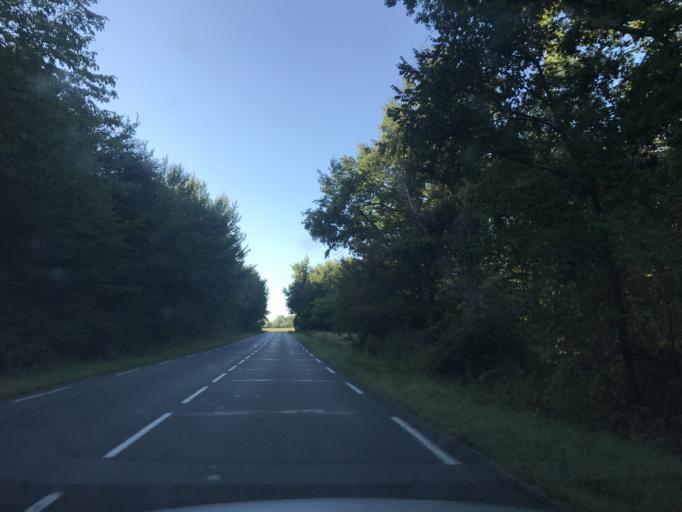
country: FR
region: Aquitaine
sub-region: Departement de la Gironde
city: Sauveterre-de-Guyenne
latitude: 44.6686
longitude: -0.1010
